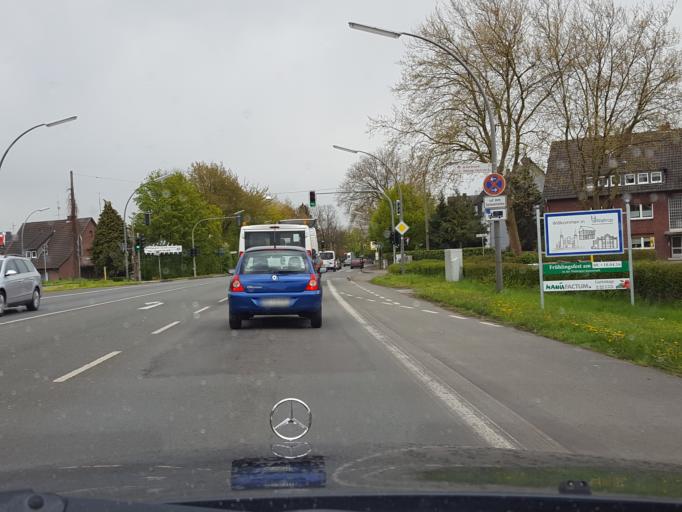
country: DE
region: North Rhine-Westphalia
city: Waltrop
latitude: 51.6252
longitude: 7.3882
